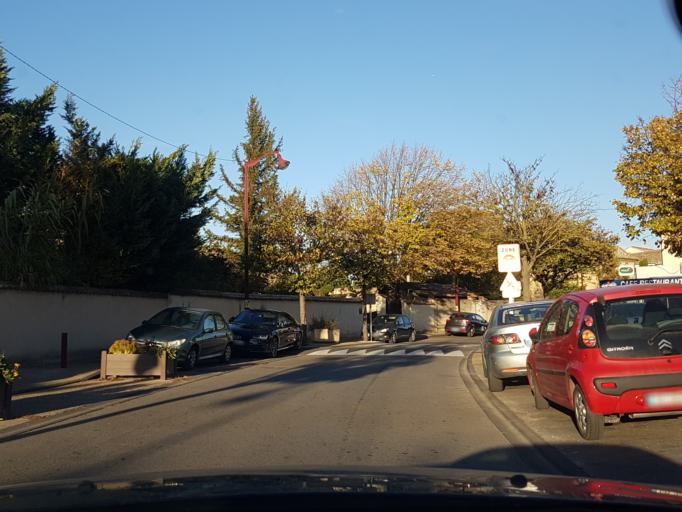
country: FR
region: Provence-Alpes-Cote d'Azur
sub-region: Departement du Vaucluse
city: Entraigues-sur-la-Sorgue
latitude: 44.0044
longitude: 4.9252
